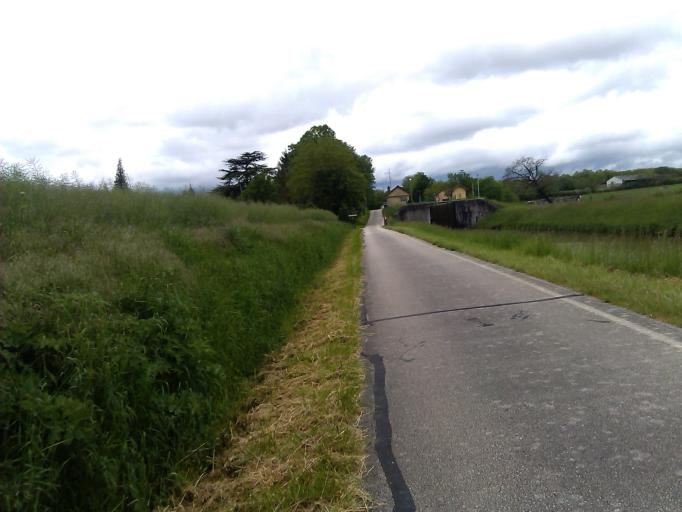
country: FR
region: Bourgogne
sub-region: Departement de Saone-et-Loire
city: Chagny
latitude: 46.8888
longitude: 4.7626
